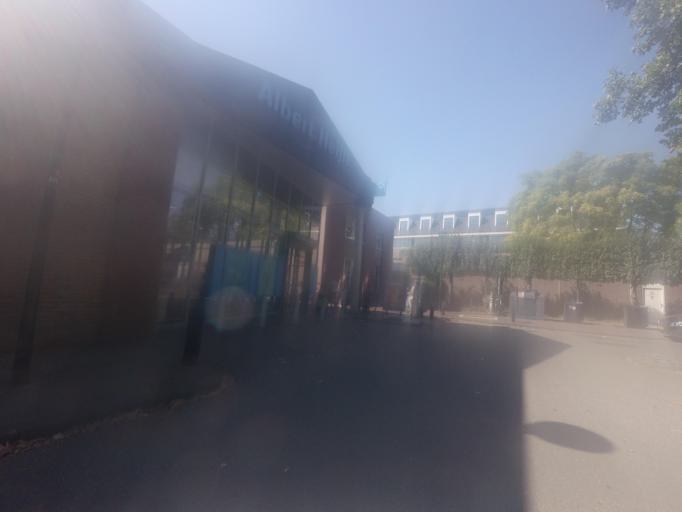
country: NL
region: North Brabant
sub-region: Gemeente Goirle
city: Goirle
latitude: 51.5213
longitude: 5.0701
